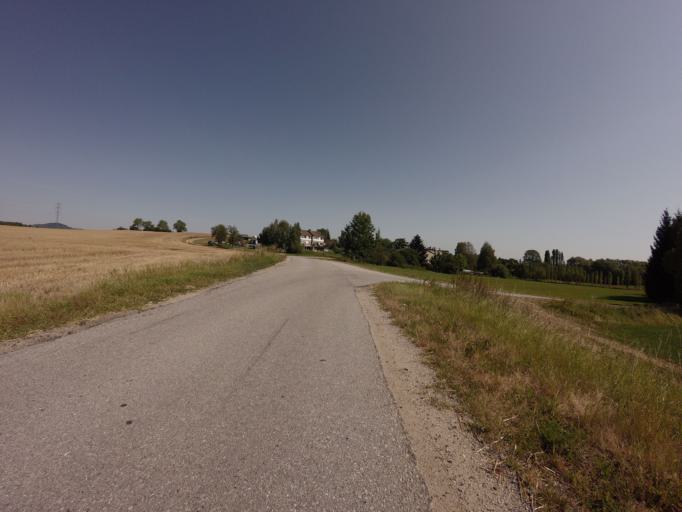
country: CZ
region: Jihocesky
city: Kamenny Ujezd
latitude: 48.8733
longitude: 14.3777
